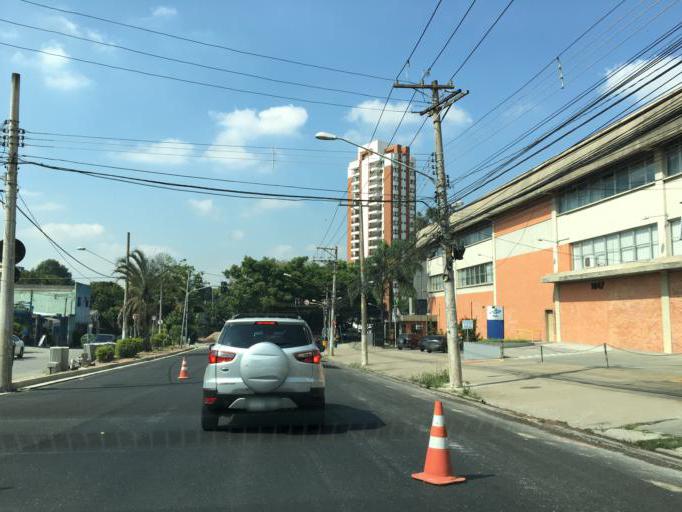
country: BR
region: Sao Paulo
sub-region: Osasco
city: Osasco
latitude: -23.5736
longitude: -46.7322
